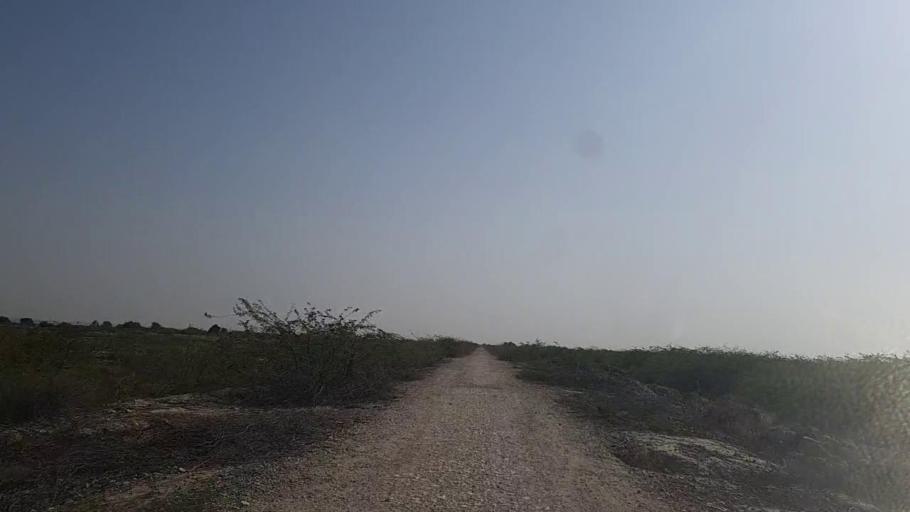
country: PK
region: Sindh
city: Naukot
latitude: 24.5983
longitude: 69.2639
